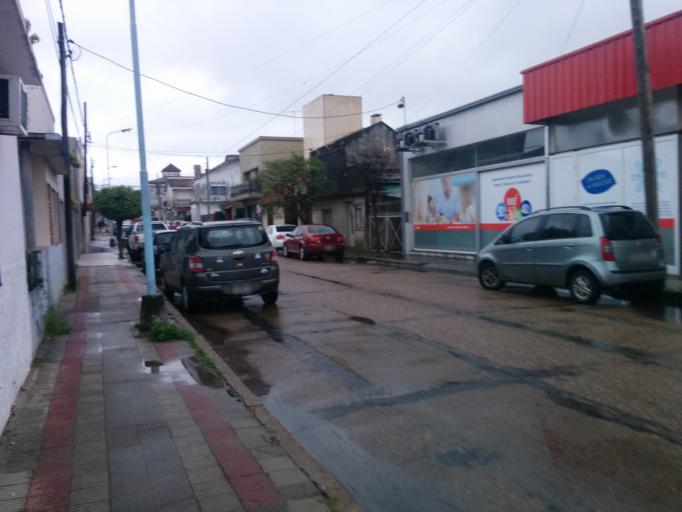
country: AR
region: Entre Rios
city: Concordia
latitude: -31.3873
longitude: -58.0145
